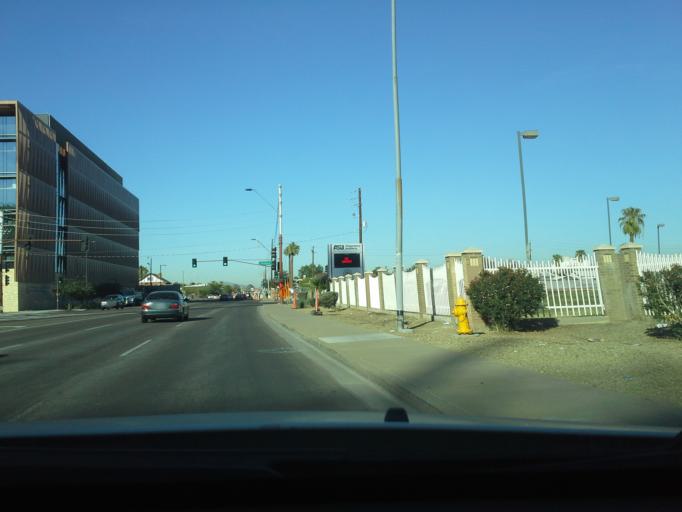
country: US
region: Arizona
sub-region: Maricopa County
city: Phoenix
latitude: 33.4538
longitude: -112.0651
